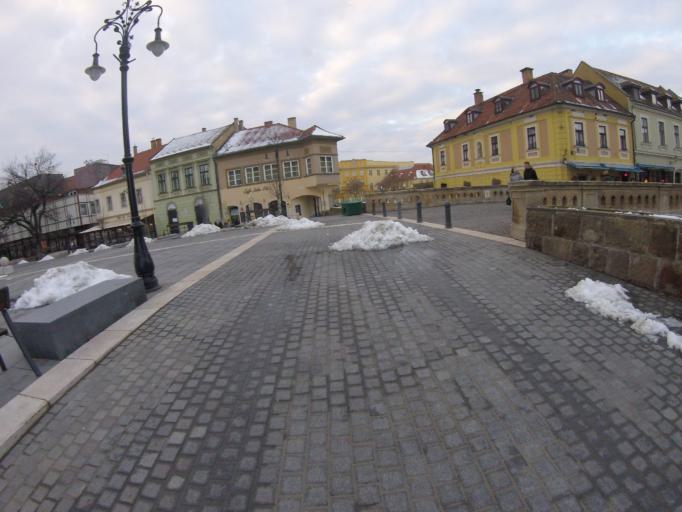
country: HU
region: Heves
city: Eger
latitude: 47.9029
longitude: 20.3776
